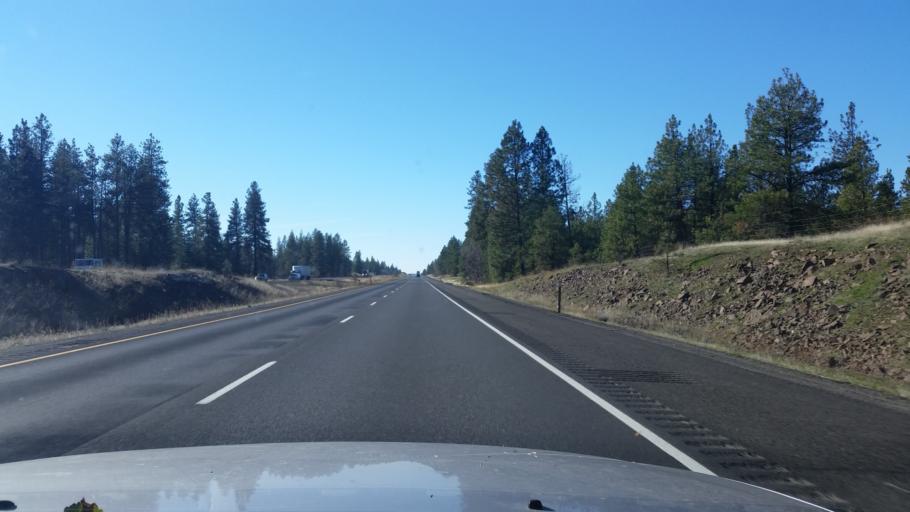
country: US
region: Washington
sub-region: Spokane County
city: Medical Lake
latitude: 47.4760
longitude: -117.7328
